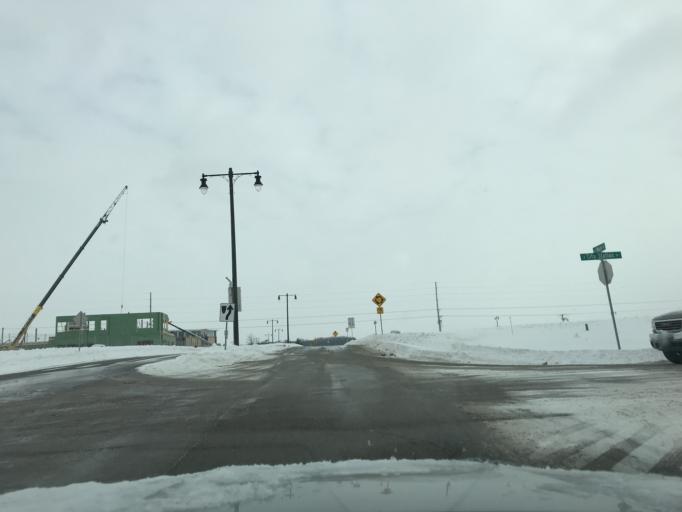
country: US
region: Wisconsin
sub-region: Dane County
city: Sun Prairie
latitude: 43.1763
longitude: -89.2672
